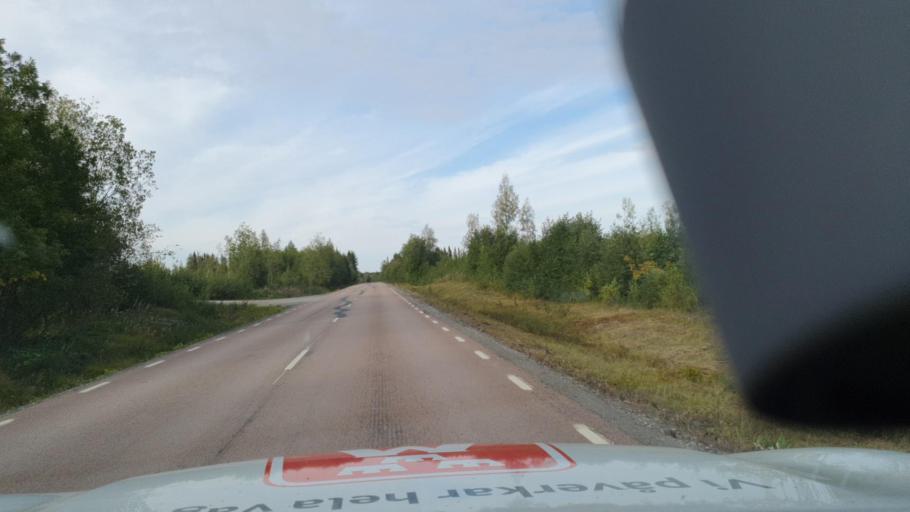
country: SE
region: Jaemtland
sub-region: Stroemsunds Kommun
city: Stroemsund
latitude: 63.7686
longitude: 15.7089
